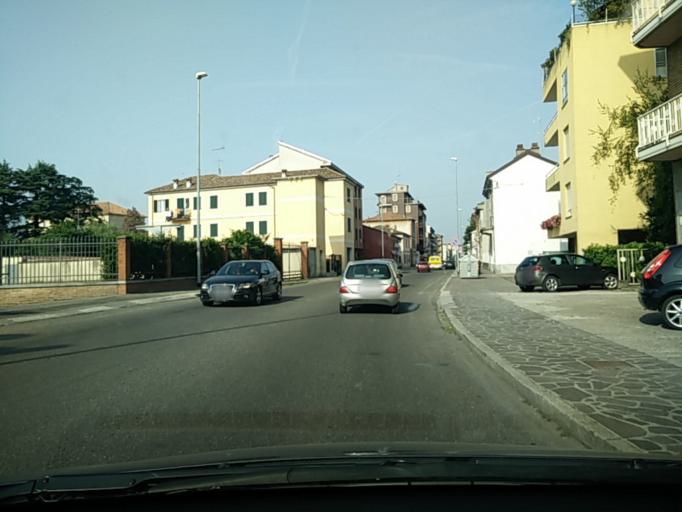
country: IT
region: Lombardy
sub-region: Provincia di Pavia
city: Casteggio
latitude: 45.0147
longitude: 9.1202
